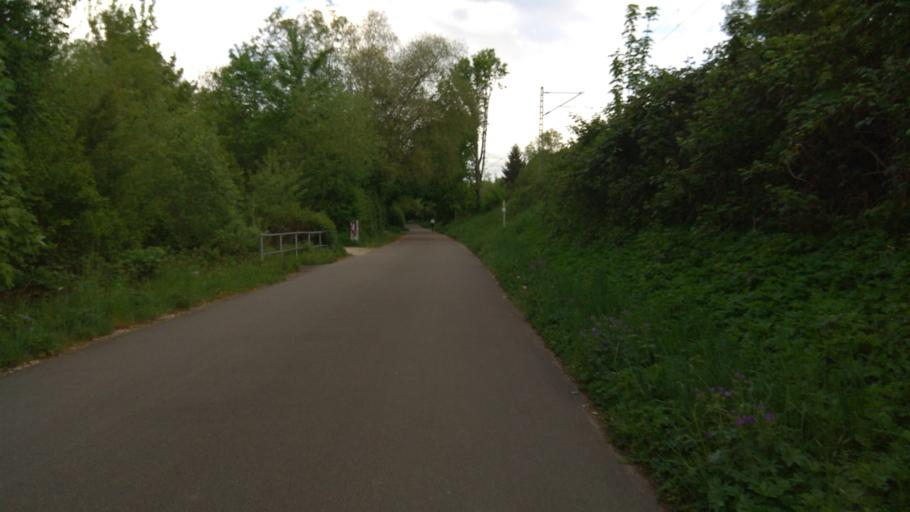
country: DE
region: Baden-Wuerttemberg
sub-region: Tuebingen Region
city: Wannweil
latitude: 48.5020
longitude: 9.1652
